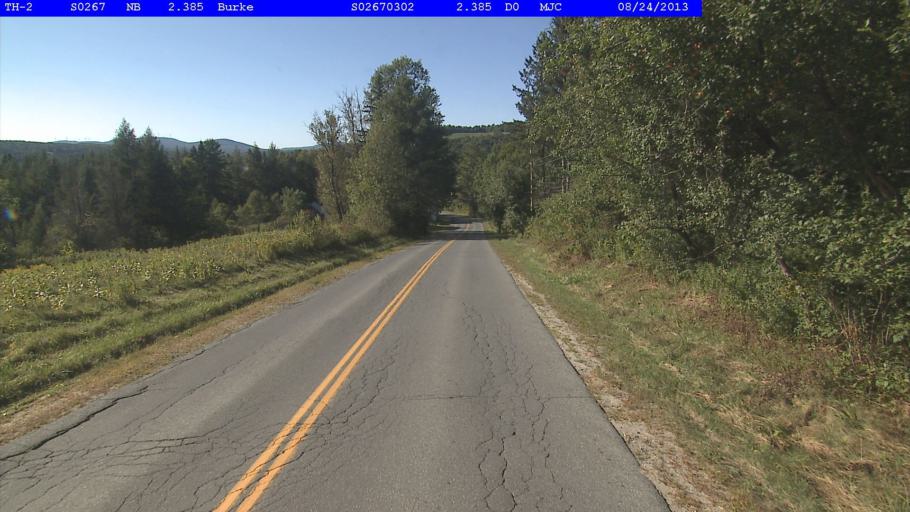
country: US
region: Vermont
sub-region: Caledonia County
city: Lyndonville
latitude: 44.6184
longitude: -71.9445
